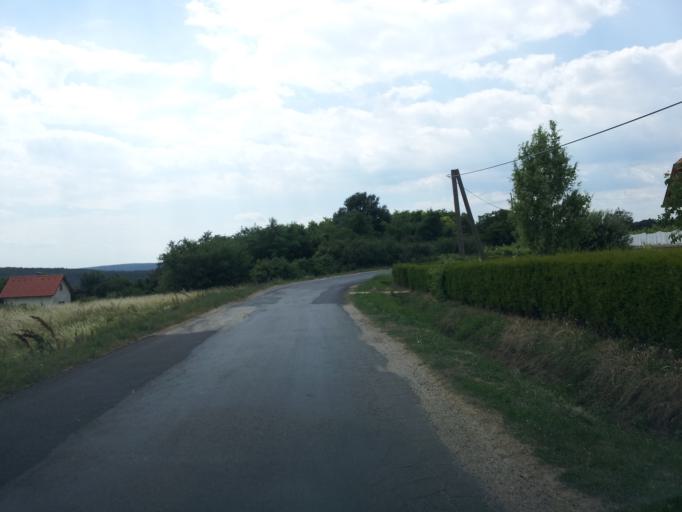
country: HU
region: Veszprem
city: Zanka
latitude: 46.9278
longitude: 17.7125
